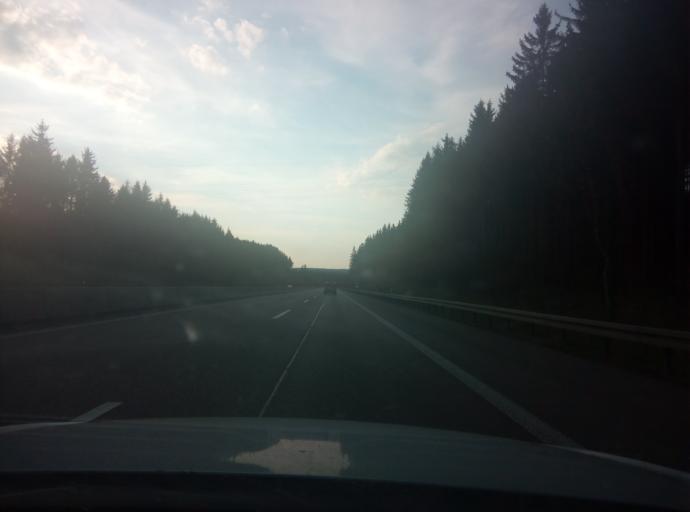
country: DE
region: Baden-Wuerttemberg
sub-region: Freiburg Region
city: Trossingen
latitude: 48.0661
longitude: 8.6121
